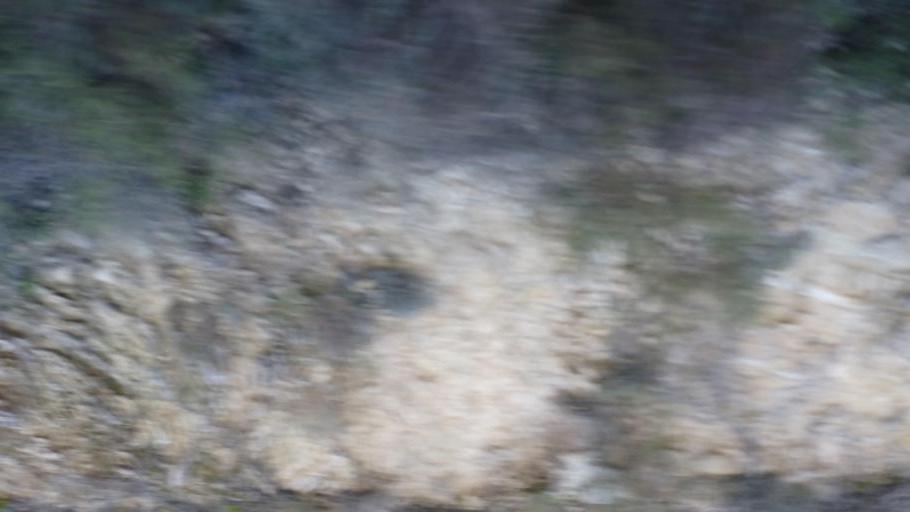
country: CY
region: Limassol
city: Pachna
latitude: 34.8128
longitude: 32.6639
